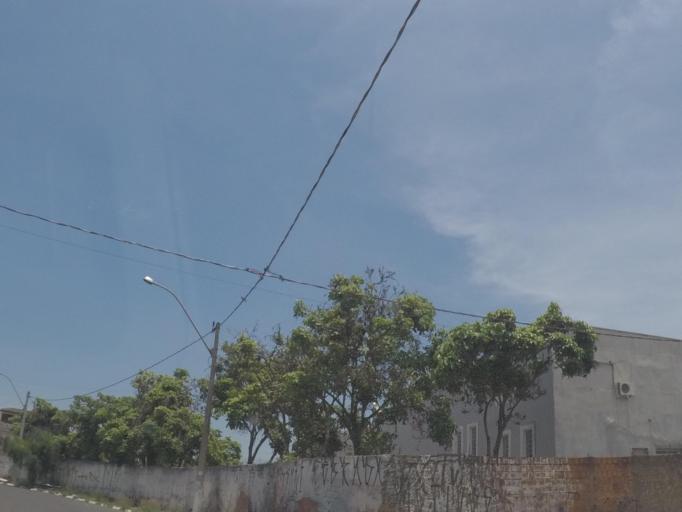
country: BR
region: Sao Paulo
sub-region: Hortolandia
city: Hortolandia
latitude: -22.8493
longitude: -47.1880
